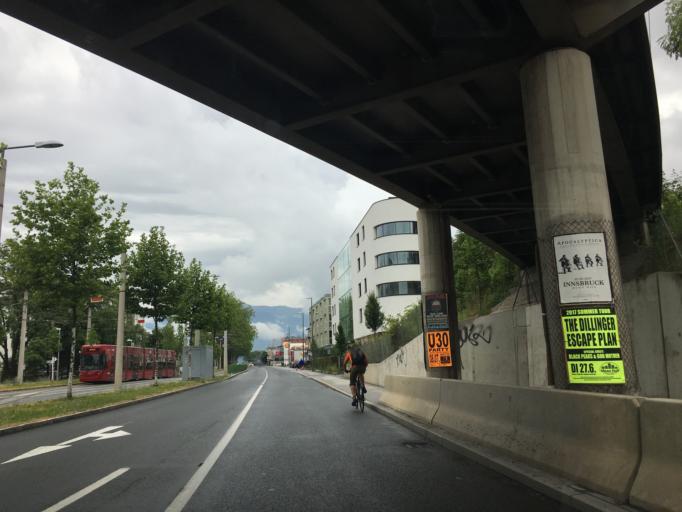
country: AT
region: Tyrol
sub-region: Innsbruck Stadt
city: Innsbruck
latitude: 47.2650
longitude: 11.3719
